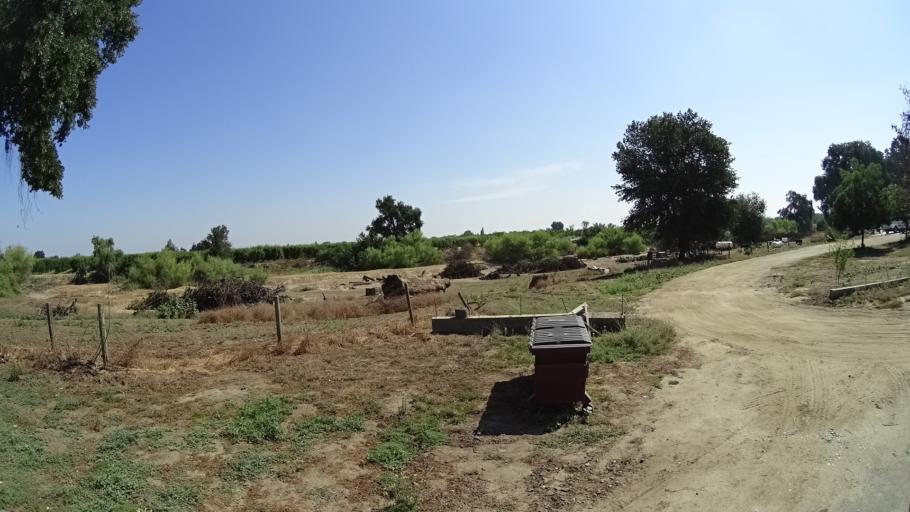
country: US
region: California
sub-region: Fresno County
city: Kingsburg
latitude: 36.4468
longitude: -119.5708
